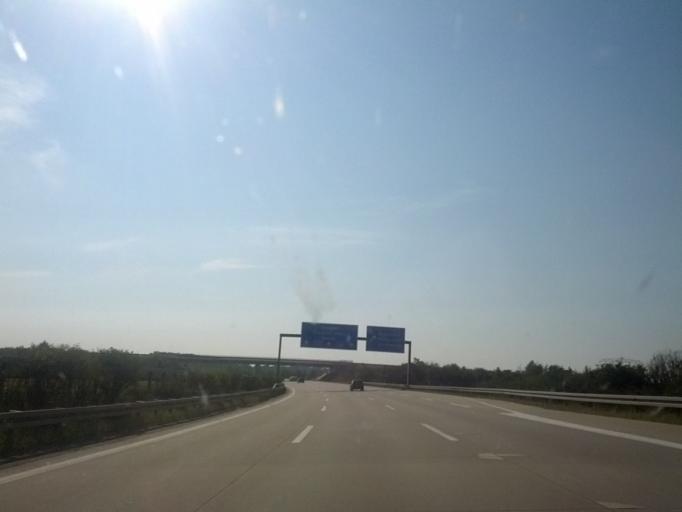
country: DE
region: Brandenburg
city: Woltersdorf
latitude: 52.4792
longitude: 13.7561
